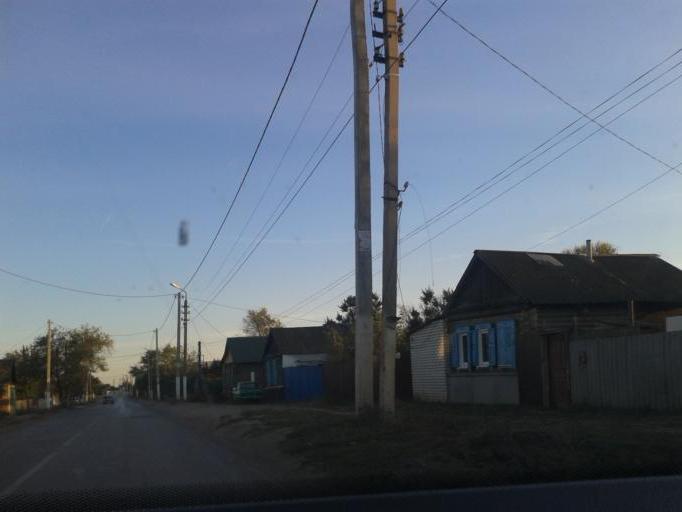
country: RU
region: Volgograd
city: Krasnoslobodsk
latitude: 48.7064
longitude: 44.5650
